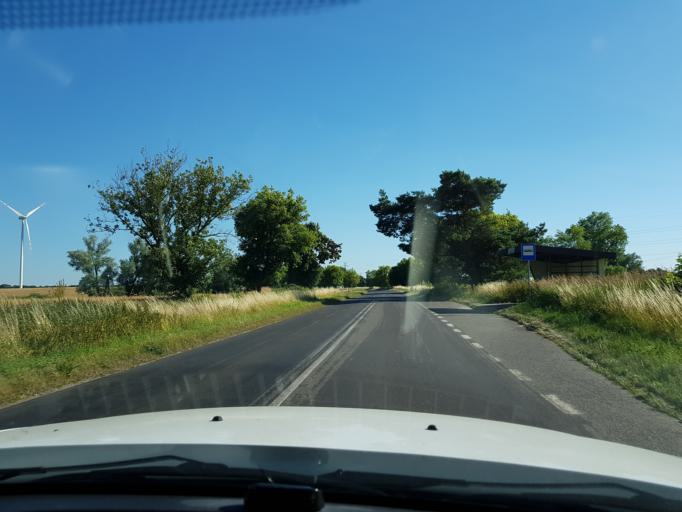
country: PL
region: West Pomeranian Voivodeship
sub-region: Powiat lobeski
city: Lobez
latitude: 53.6777
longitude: 15.6045
